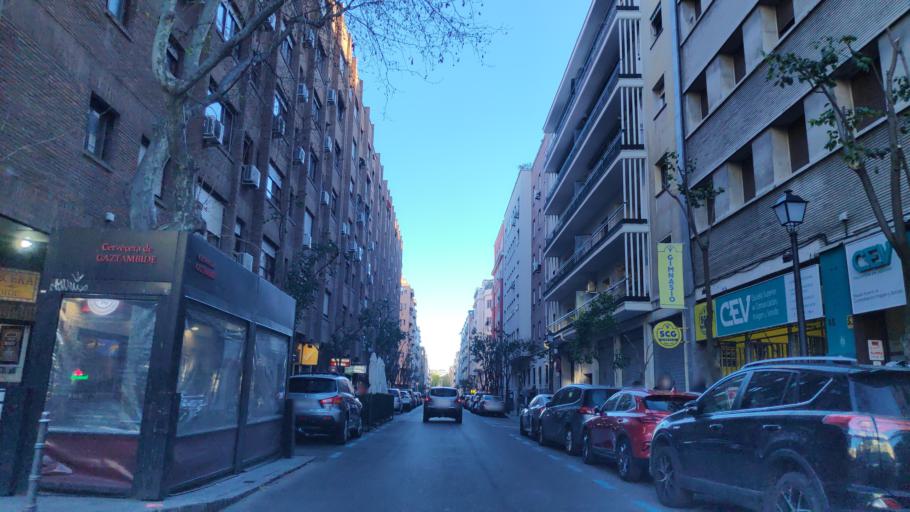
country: ES
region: Madrid
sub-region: Provincia de Madrid
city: Chamberi
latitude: 40.4375
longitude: -3.7154
